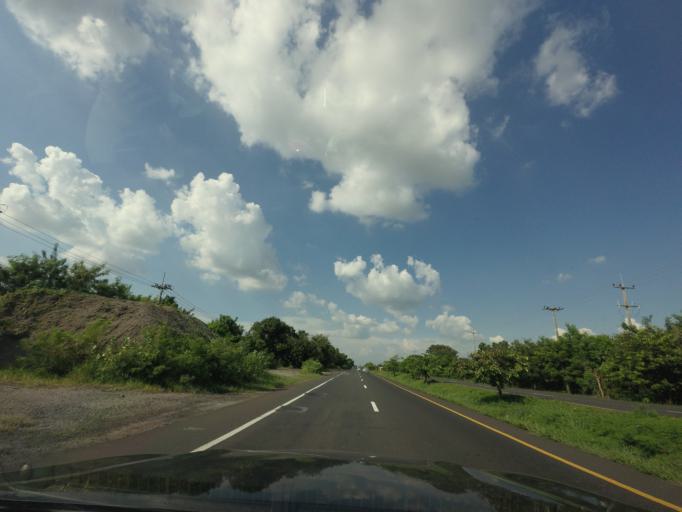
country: TH
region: Nakhon Ratchasima
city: Bua Lai
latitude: 15.6919
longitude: 102.5807
